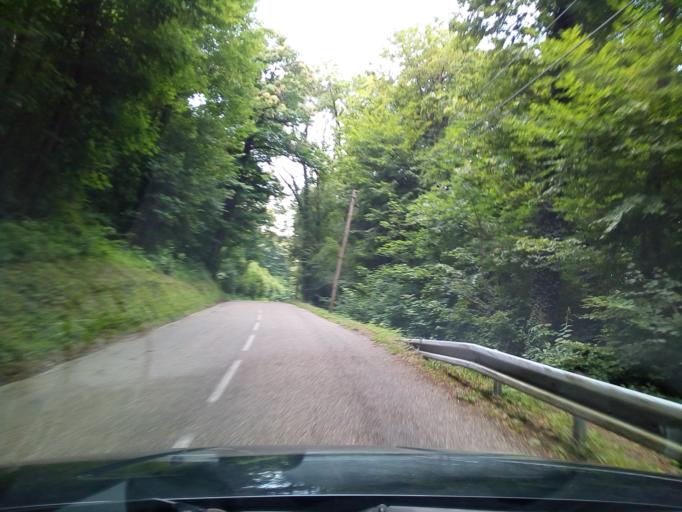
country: FR
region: Rhone-Alpes
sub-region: Departement de l'Isere
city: Gieres
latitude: 45.1756
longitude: 5.7768
